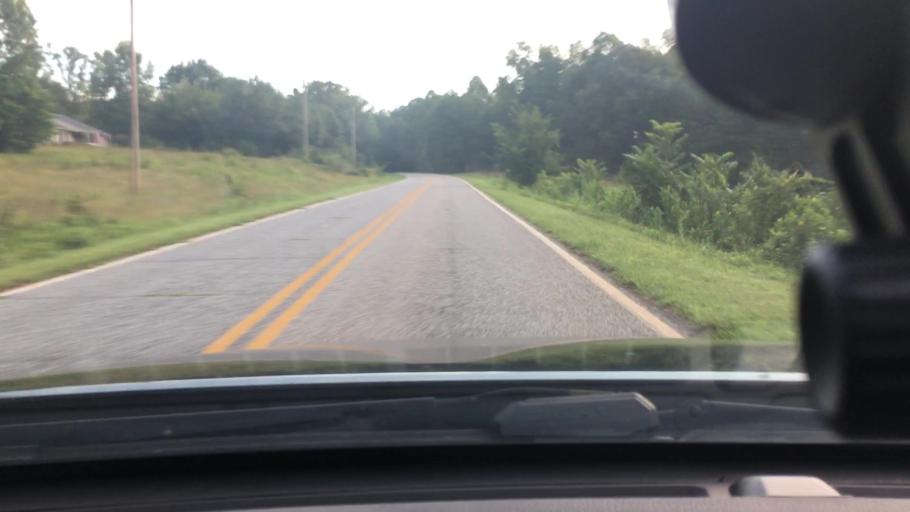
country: US
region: North Carolina
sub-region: Rutherford County
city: Rutherfordton
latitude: 35.3843
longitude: -81.9853
